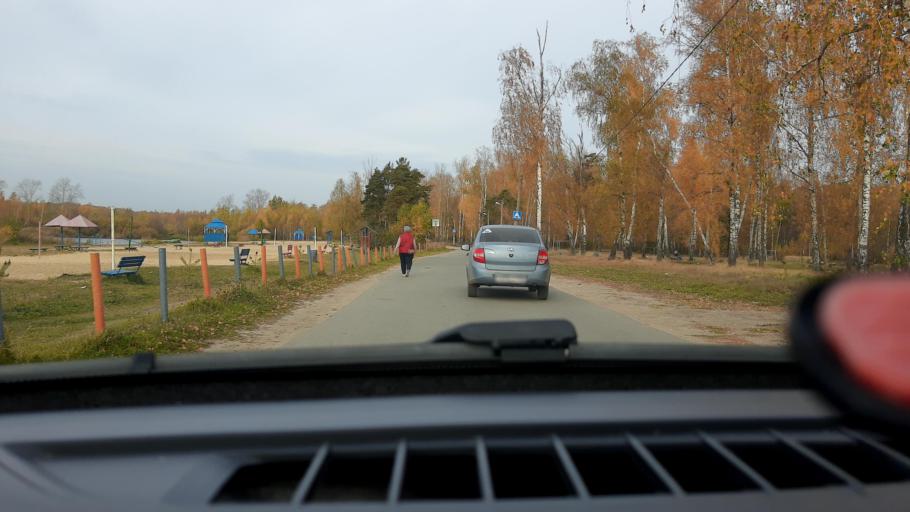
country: RU
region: Nizjnij Novgorod
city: Gorbatovka
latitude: 56.2929
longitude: 43.8372
